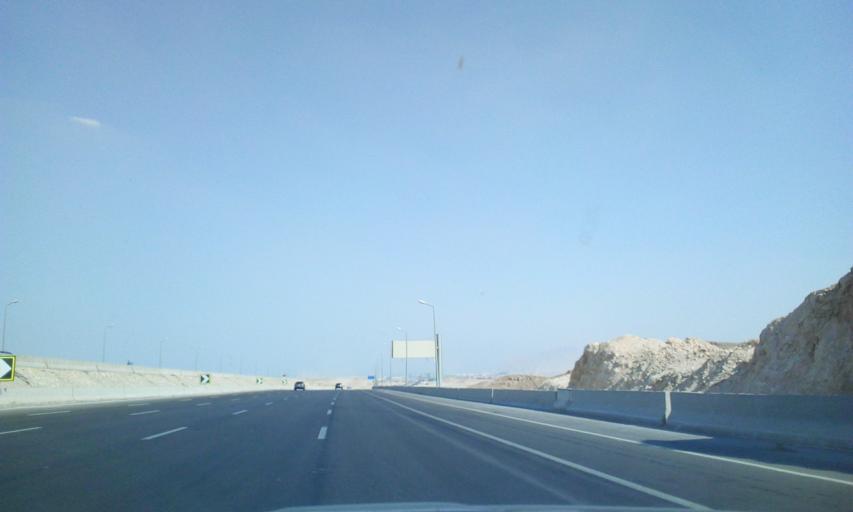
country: EG
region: As Suways
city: Ain Sukhna
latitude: 29.6779
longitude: 32.2239
